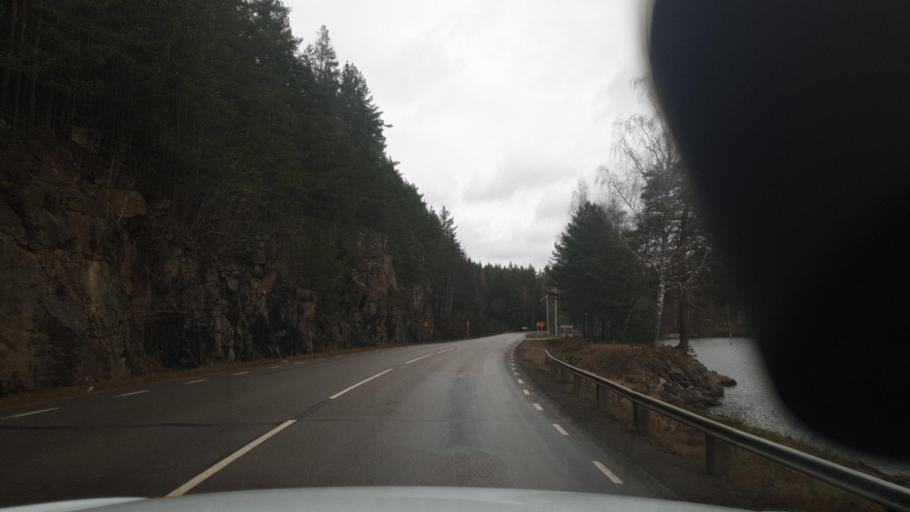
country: SE
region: Vaermland
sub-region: Arvika Kommun
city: Arvika
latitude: 59.7187
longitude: 12.6279
